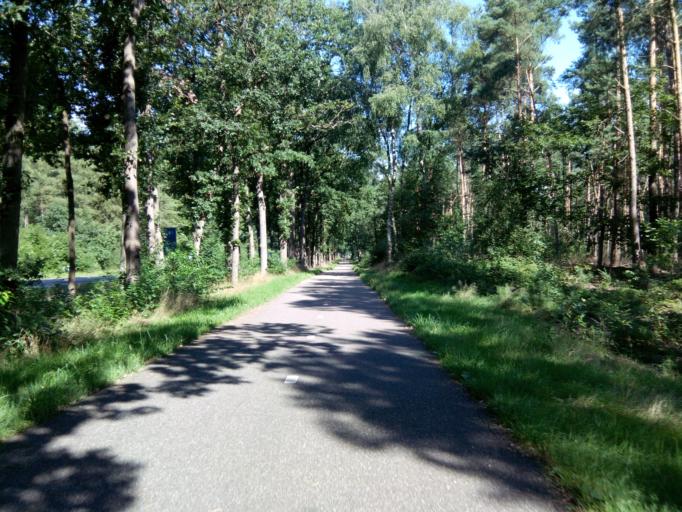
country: NL
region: Utrecht
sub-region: Gemeente Utrechtse Heuvelrug
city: Maarn
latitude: 52.0794
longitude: 5.3606
